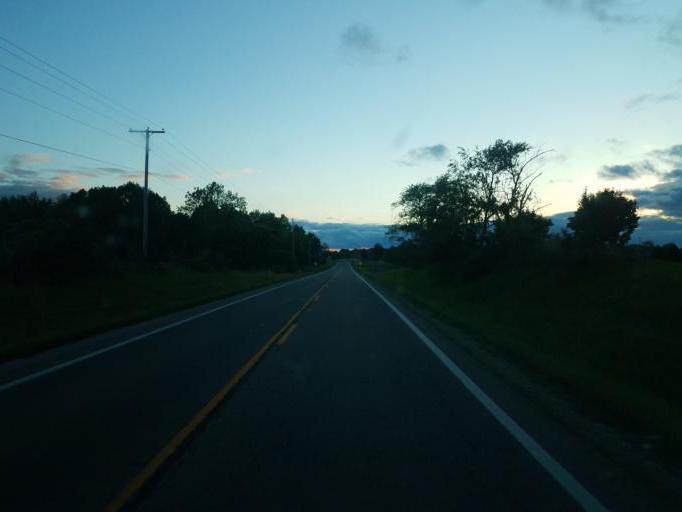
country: US
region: Ohio
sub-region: Morrow County
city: Mount Gilead
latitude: 40.5595
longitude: -82.8015
